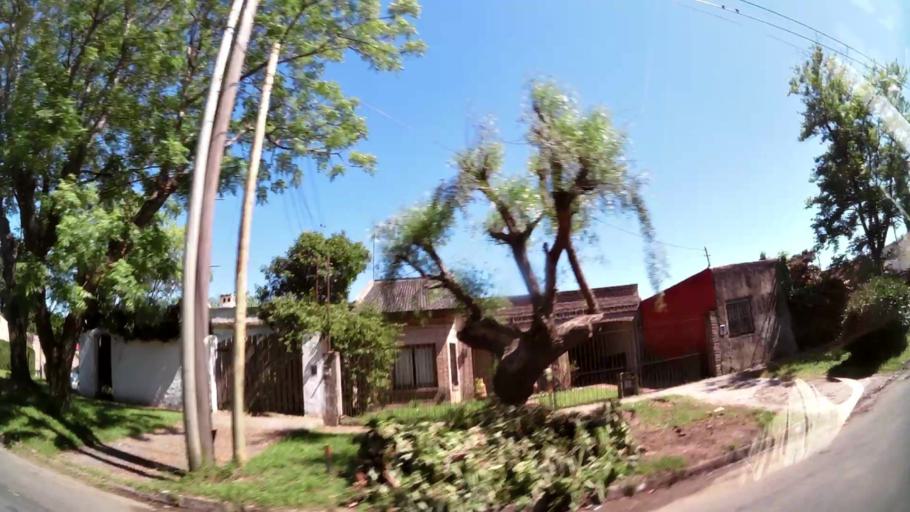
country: AR
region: Buenos Aires
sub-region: Partido de Tigre
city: Tigre
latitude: -34.4974
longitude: -58.6248
